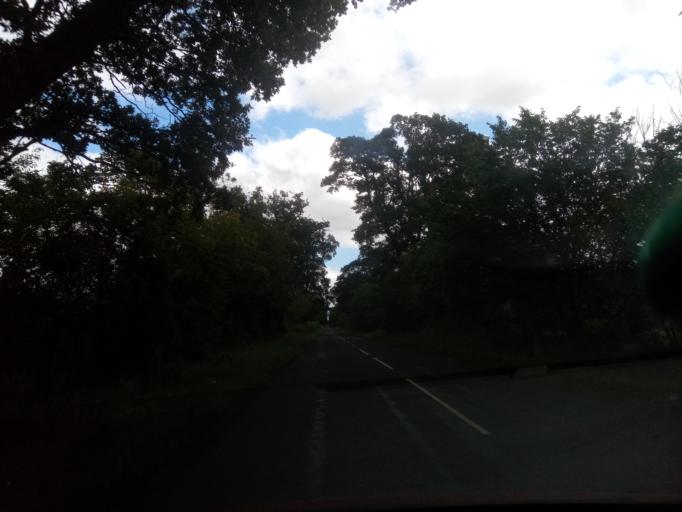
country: GB
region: Scotland
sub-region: The Scottish Borders
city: Kelso
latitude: 55.6035
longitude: -2.4112
